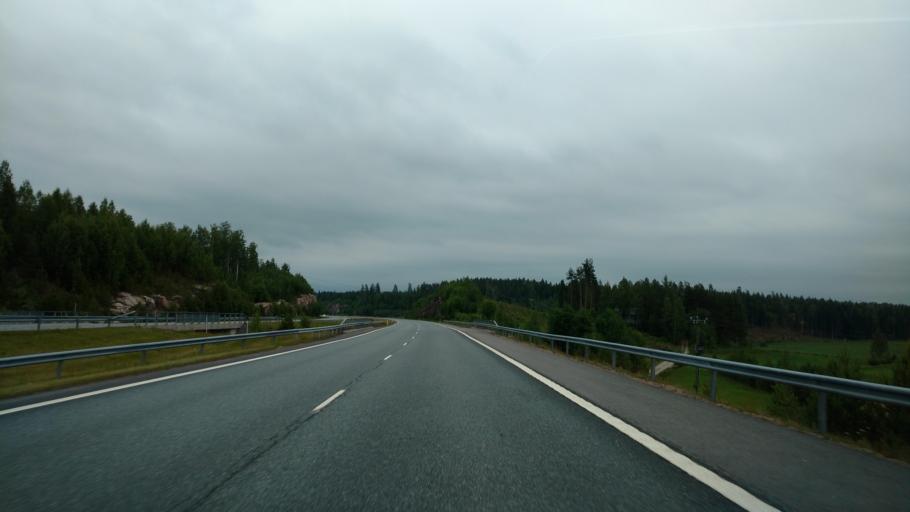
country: FI
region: Varsinais-Suomi
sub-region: Salo
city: Pertteli
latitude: 60.4027
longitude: 23.2269
